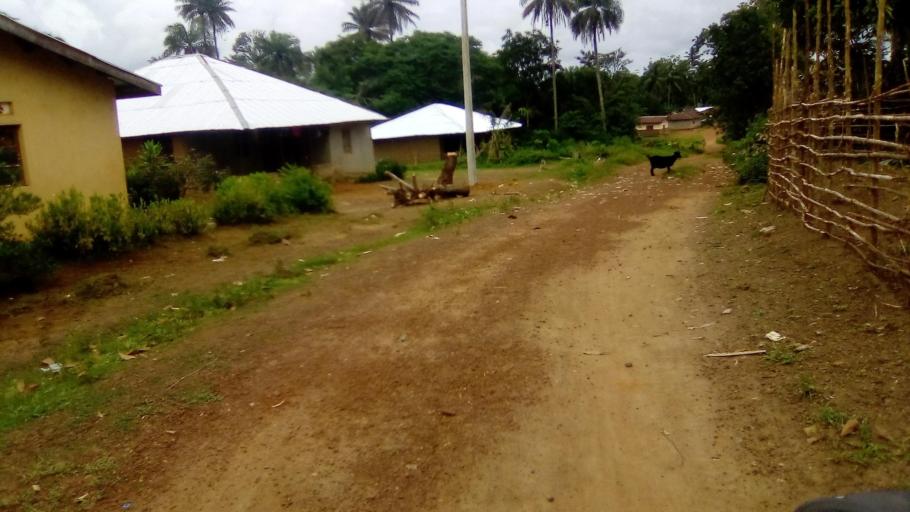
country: SL
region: Southern Province
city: Pujehun
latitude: 7.3721
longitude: -11.7116
